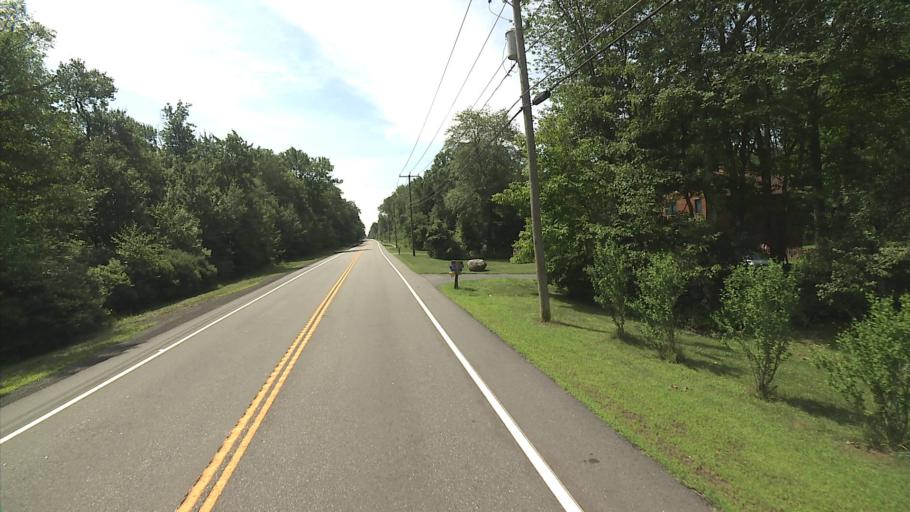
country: US
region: Connecticut
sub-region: Tolland County
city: Tolland
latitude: 41.8223
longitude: -72.3979
